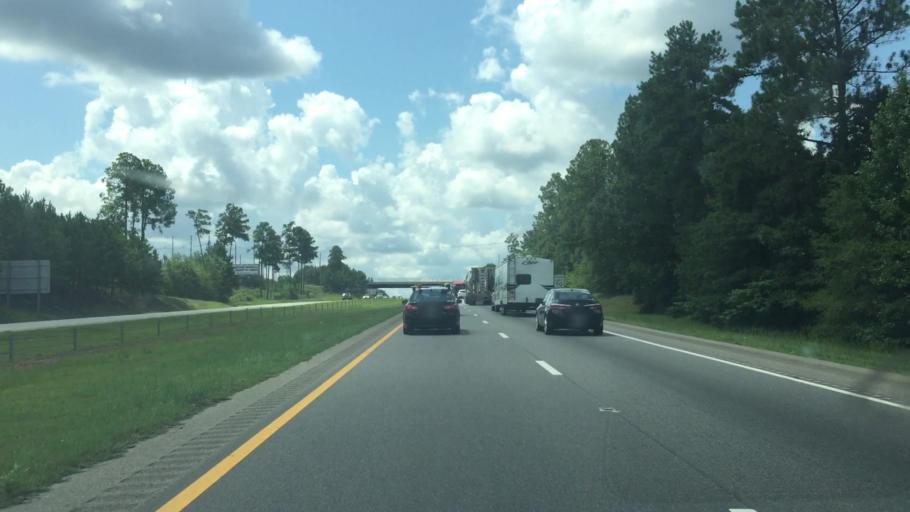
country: US
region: North Carolina
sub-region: Richmond County
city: East Rockingham
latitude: 34.9029
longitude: -79.7903
